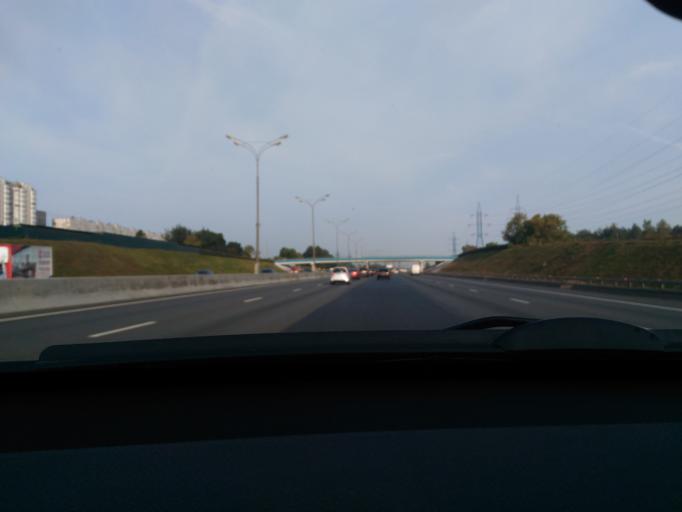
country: RU
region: Moscow
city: Bibirevo
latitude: 55.9017
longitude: 37.6194
